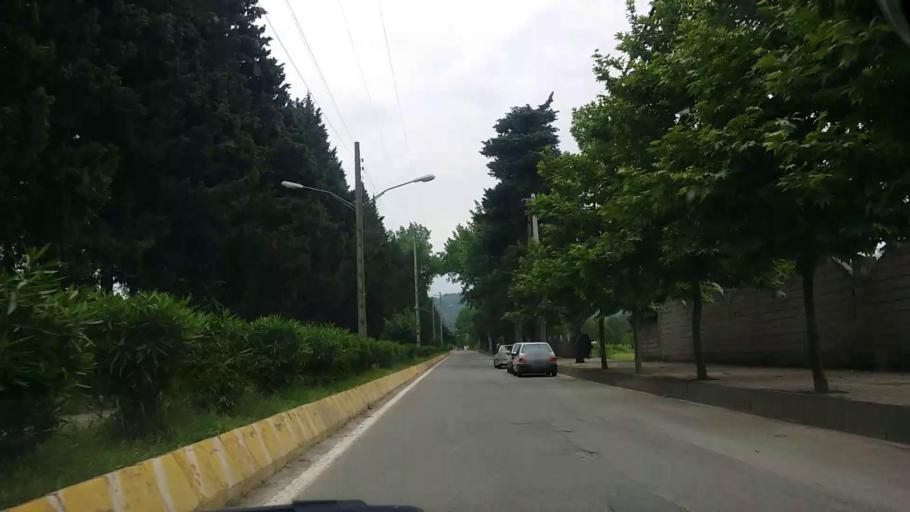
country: IR
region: Mazandaran
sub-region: Nowshahr
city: Nowshahr
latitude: 36.6332
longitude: 51.5026
